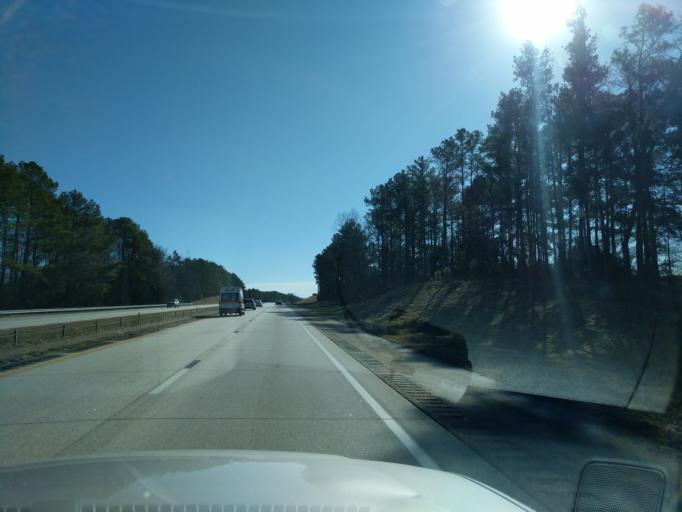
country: US
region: South Carolina
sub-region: Laurens County
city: Laurens
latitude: 34.6087
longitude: -82.0710
